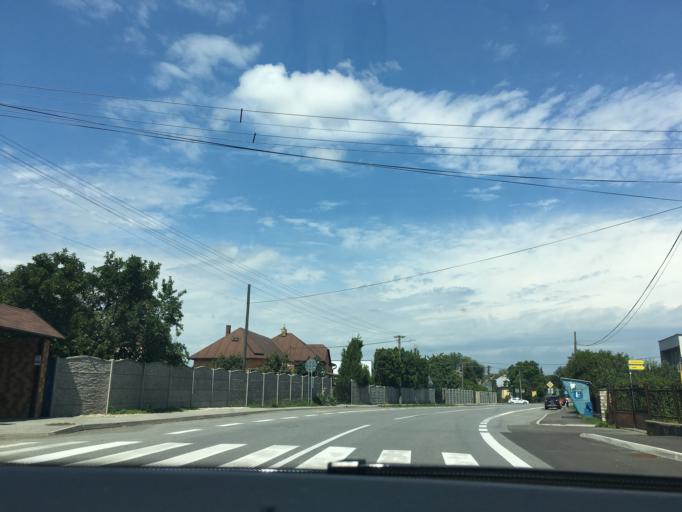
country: SK
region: Presovsky
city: Vranov nad Topl'ou
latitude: 48.8201
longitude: 21.6882
